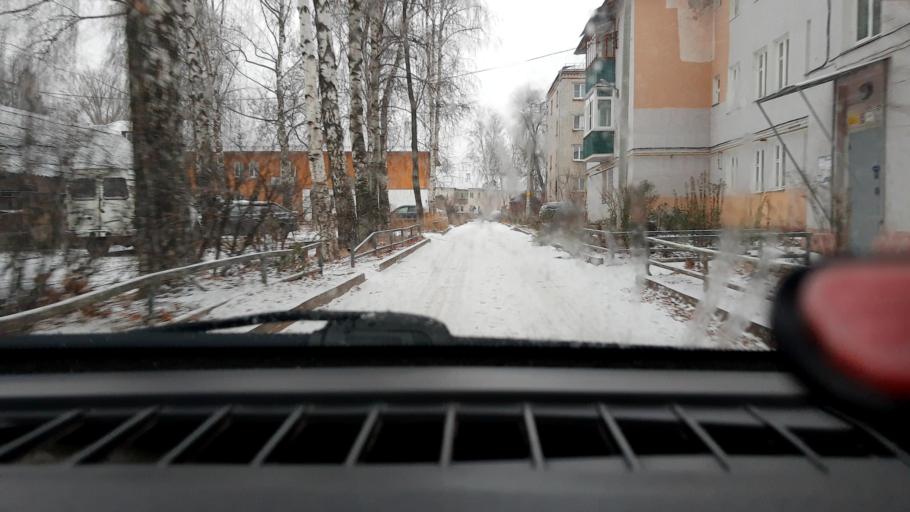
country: RU
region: Nizjnij Novgorod
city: Kstovo
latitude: 56.1468
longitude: 44.2010
